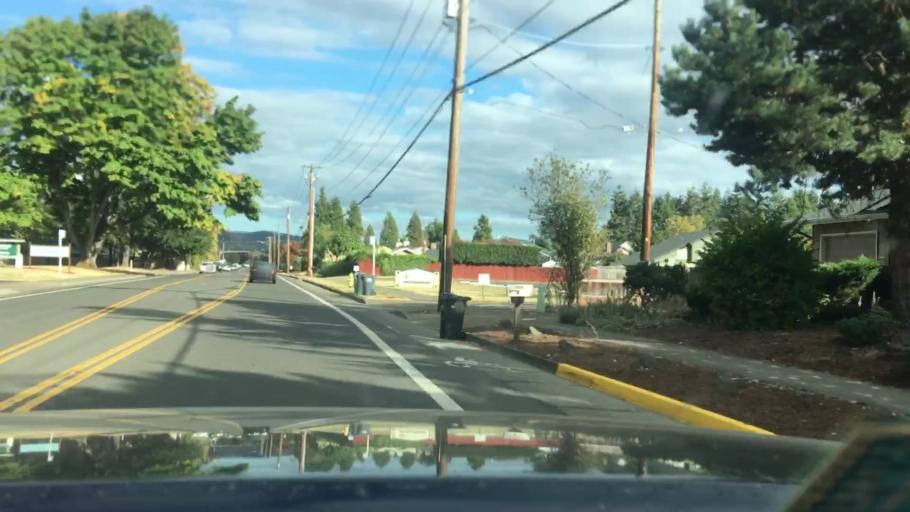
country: US
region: Oregon
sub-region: Lane County
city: Eugene
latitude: 44.0929
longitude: -123.0729
